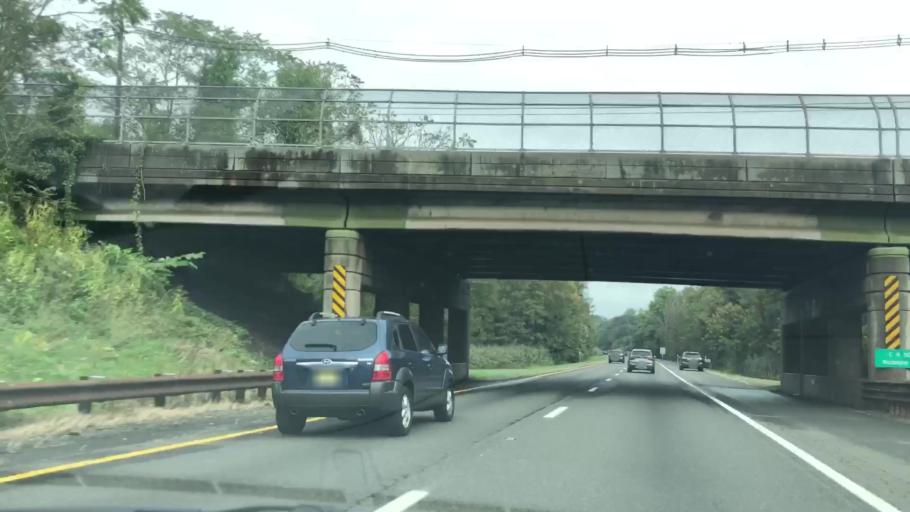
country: US
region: New Jersey
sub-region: Bergen County
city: Woodcliff Lake
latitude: 40.9986
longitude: -74.0711
